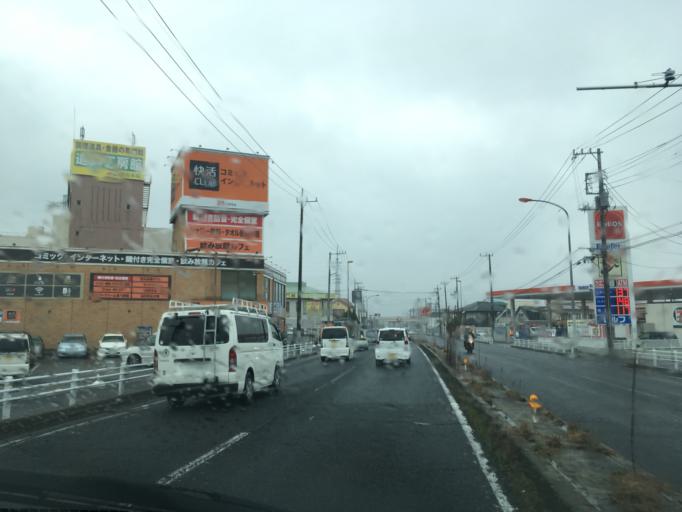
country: JP
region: Saitama
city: Koshigaya
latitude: 35.8768
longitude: 139.7773
